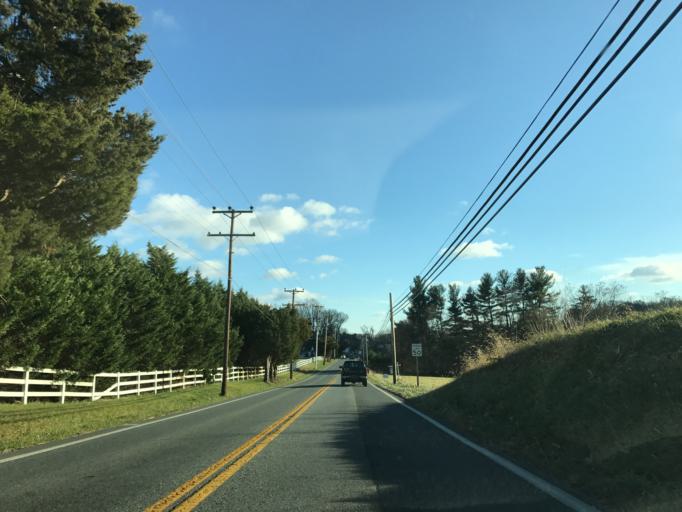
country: US
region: Maryland
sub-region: Harford County
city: Jarrettsville
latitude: 39.6234
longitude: -76.5501
